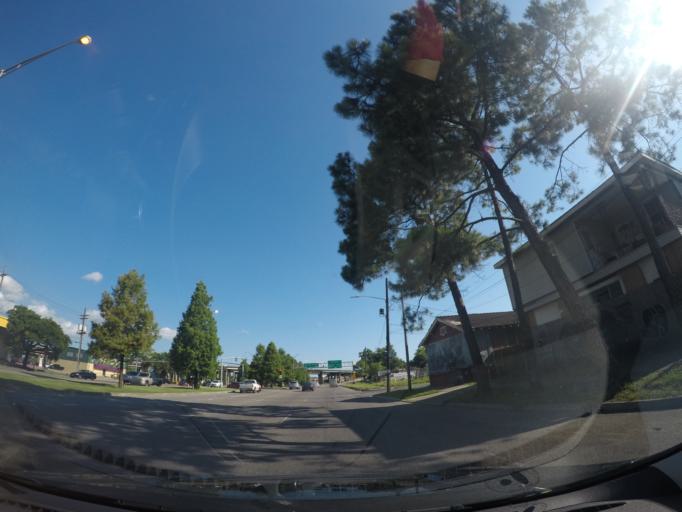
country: US
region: Louisiana
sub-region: Orleans Parish
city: New Orleans
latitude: 29.9831
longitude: -90.0581
